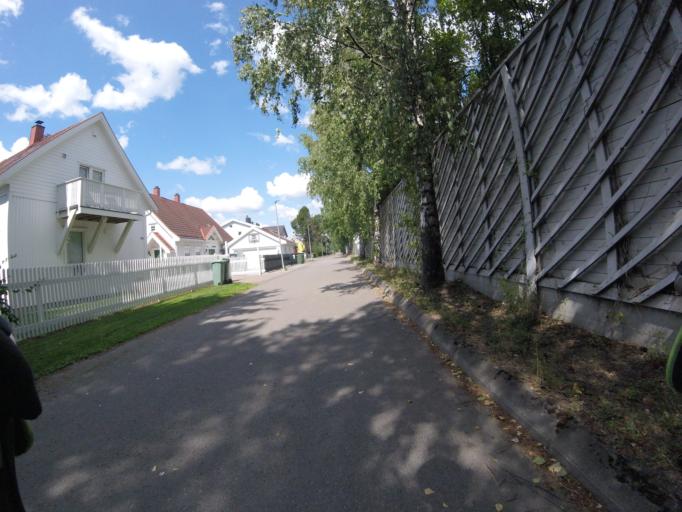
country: NO
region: Akershus
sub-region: Skedsmo
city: Lillestrom
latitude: 59.9587
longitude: 11.0675
